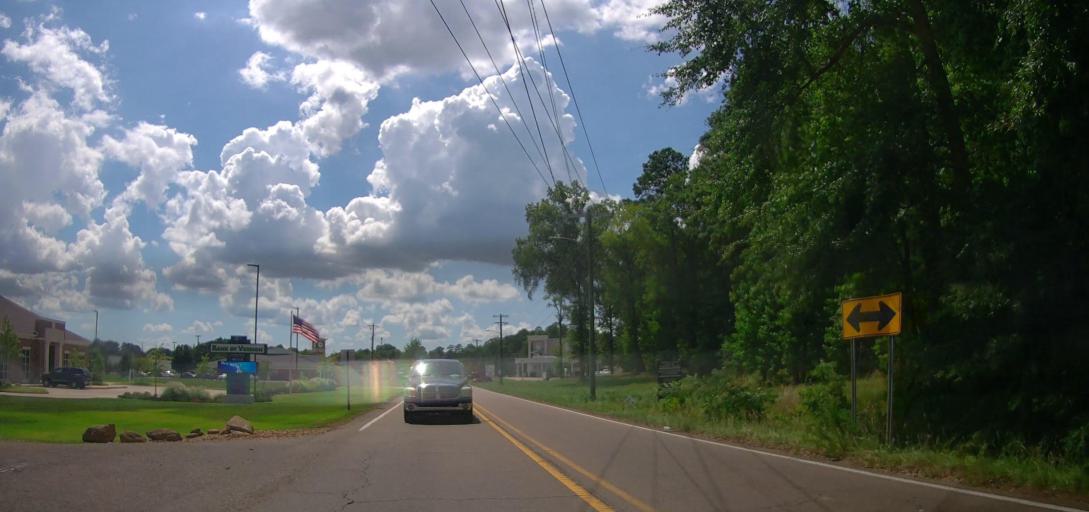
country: US
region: Mississippi
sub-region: Lowndes County
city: Columbus
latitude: 33.5381
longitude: -88.4351
